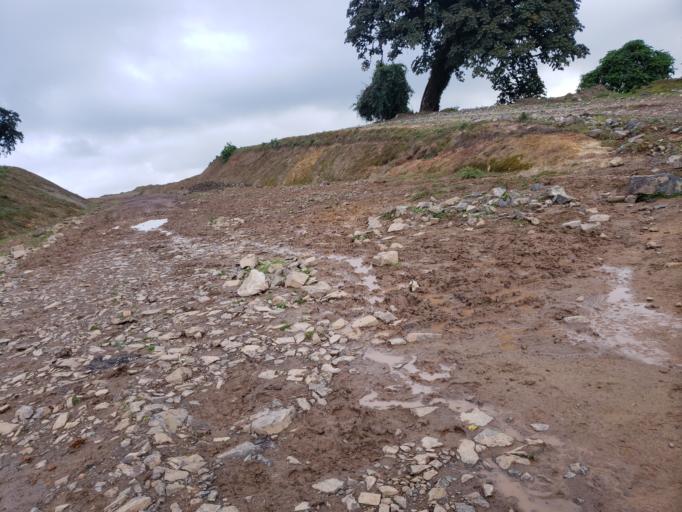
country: ET
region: Oromiya
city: Dodola
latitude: 6.6593
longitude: 39.3635
